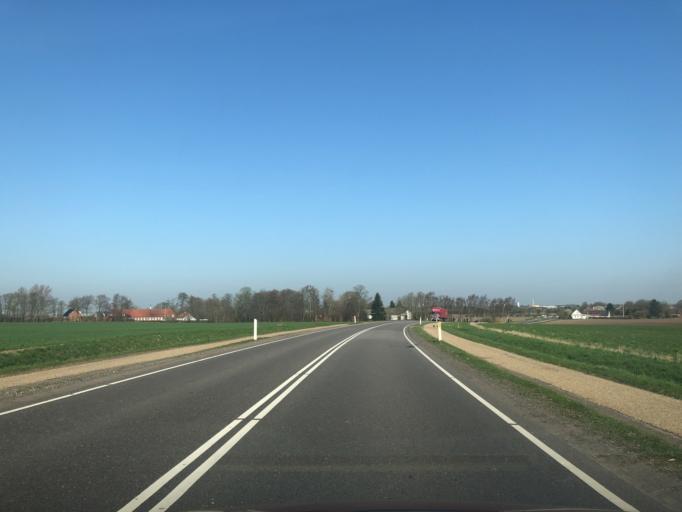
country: DK
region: Zealand
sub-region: Ringsted Kommune
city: Ringsted
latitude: 55.4189
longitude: 11.8271
